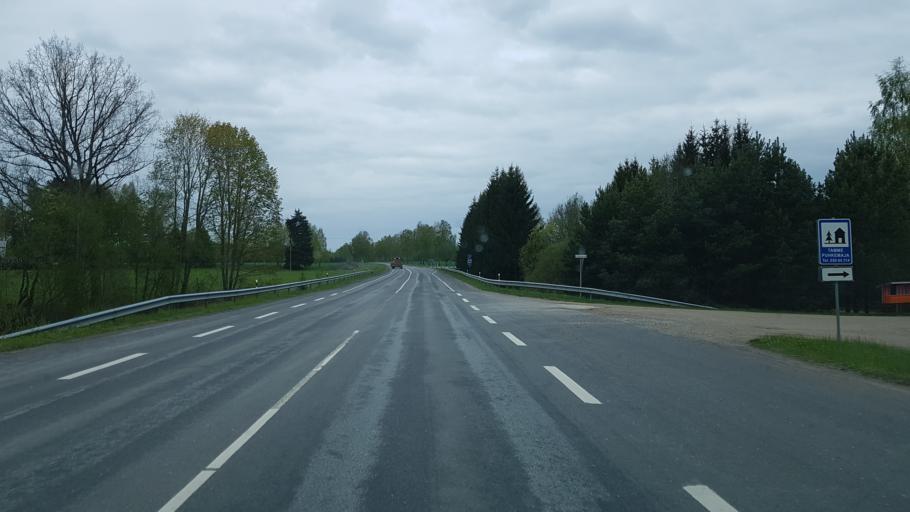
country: EE
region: Viljandimaa
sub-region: Viljandi linn
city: Viljandi
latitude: 58.3244
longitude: 25.5755
